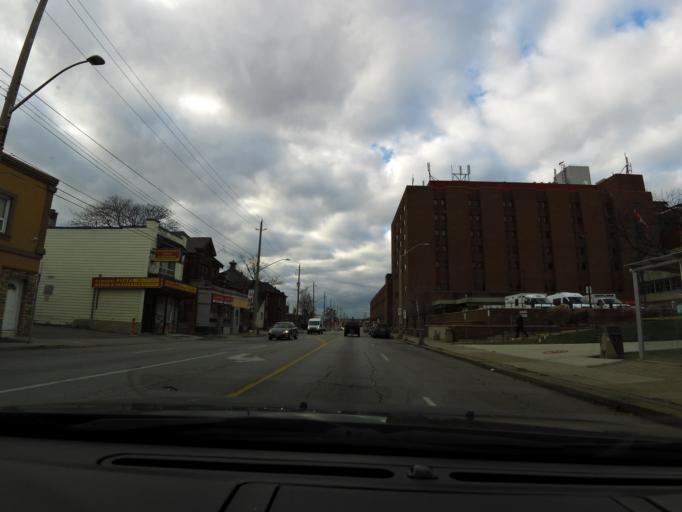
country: CA
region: Ontario
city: Hamilton
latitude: 43.2611
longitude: -79.8535
